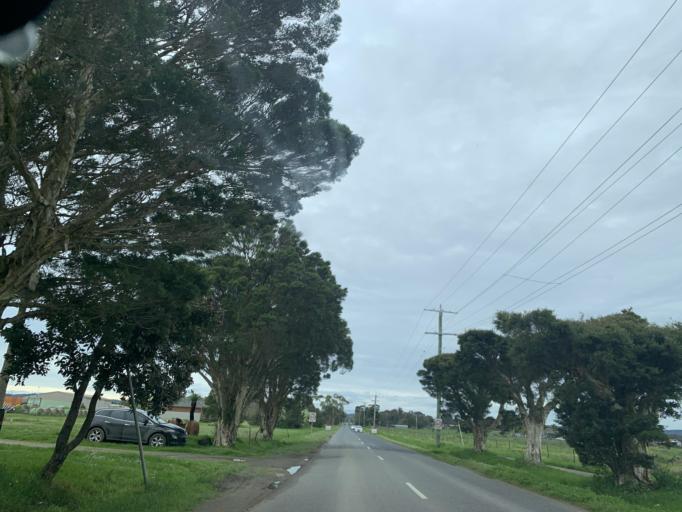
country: AU
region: Victoria
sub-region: Cardinia
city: Pakenham South
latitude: -38.0802
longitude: 145.5704
